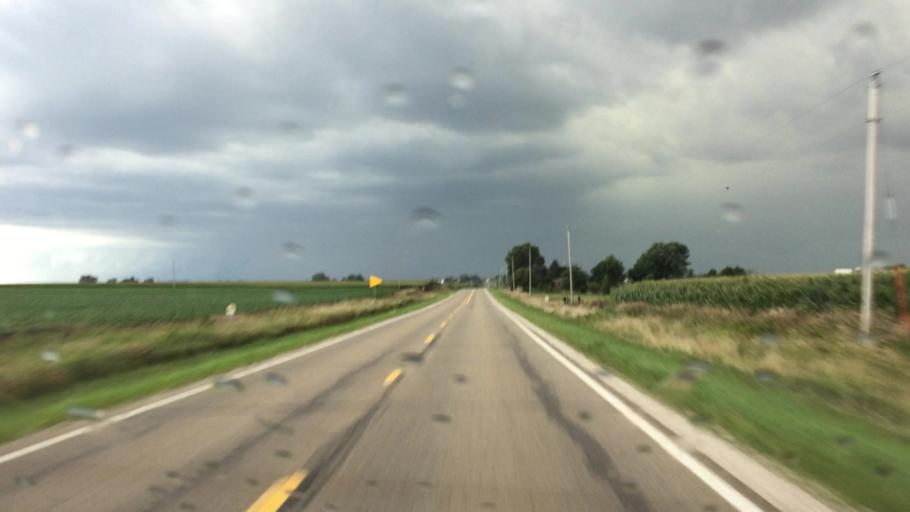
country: US
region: Iowa
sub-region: Henry County
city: Mount Pleasant
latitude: 40.7843
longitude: -91.5214
